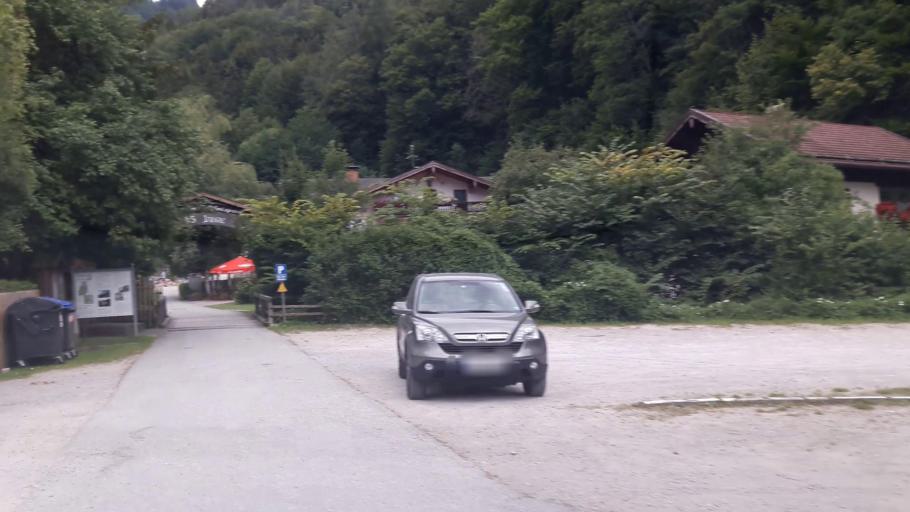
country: DE
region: Bavaria
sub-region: Upper Bavaria
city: Grassau
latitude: 47.7653
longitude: 12.4410
